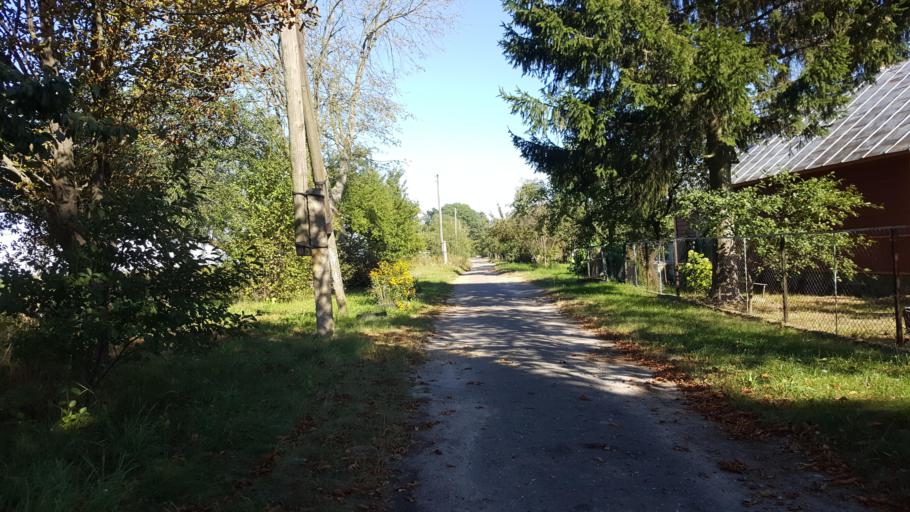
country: PL
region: Lublin Voivodeship
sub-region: Powiat bialski
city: Janow Podlaski
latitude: 52.2401
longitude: 23.2383
